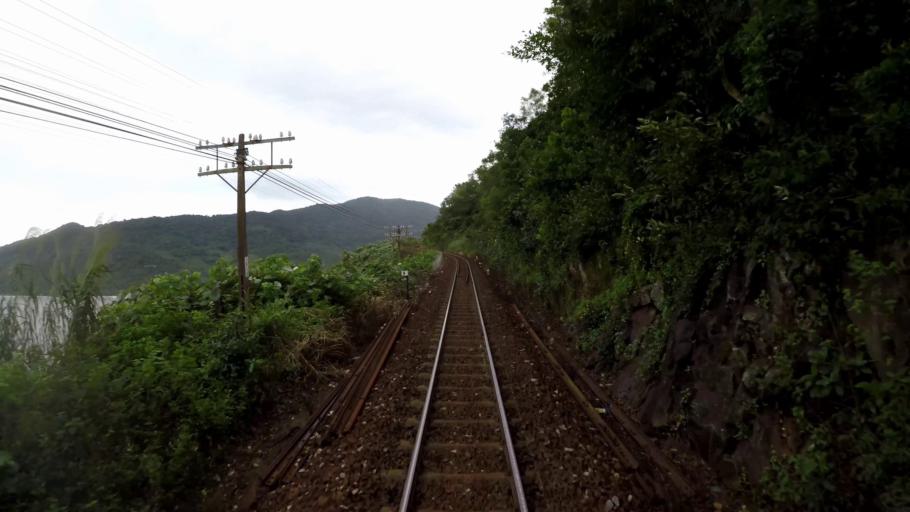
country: VN
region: Da Nang
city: Lien Chieu
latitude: 16.2137
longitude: 108.1339
